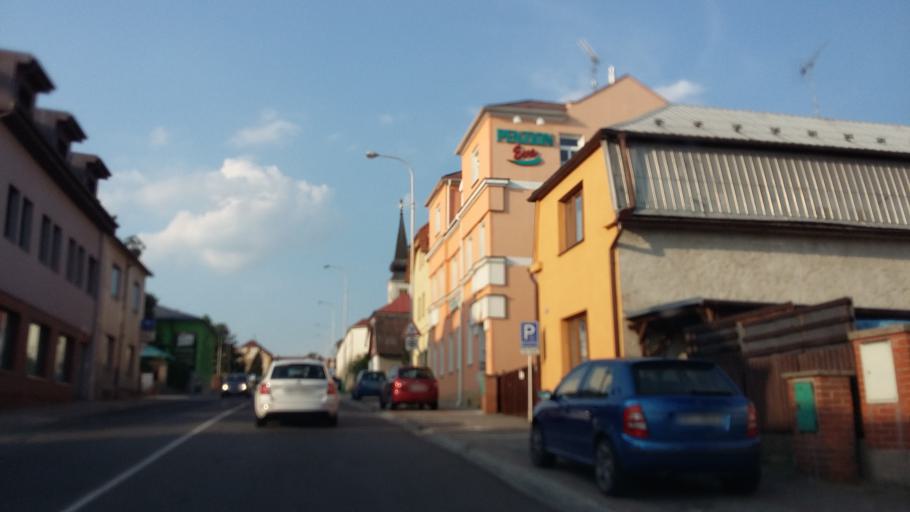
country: CZ
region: Central Bohemia
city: Kosmonosy
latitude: 50.4372
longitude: 14.9294
